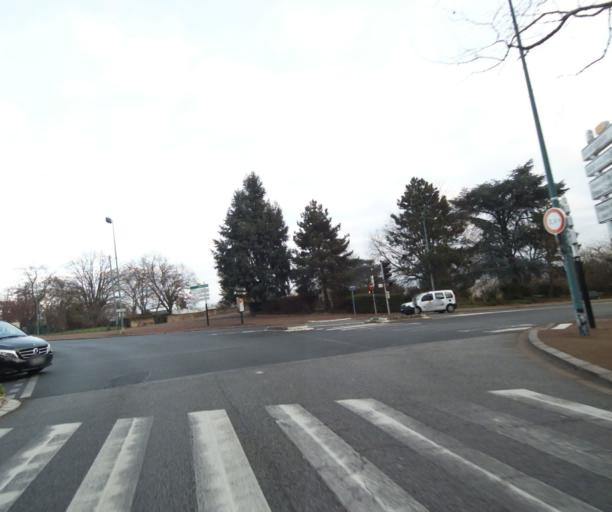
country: FR
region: Ile-de-France
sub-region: Departement des Hauts-de-Seine
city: Suresnes
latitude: 48.8754
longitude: 2.2179
